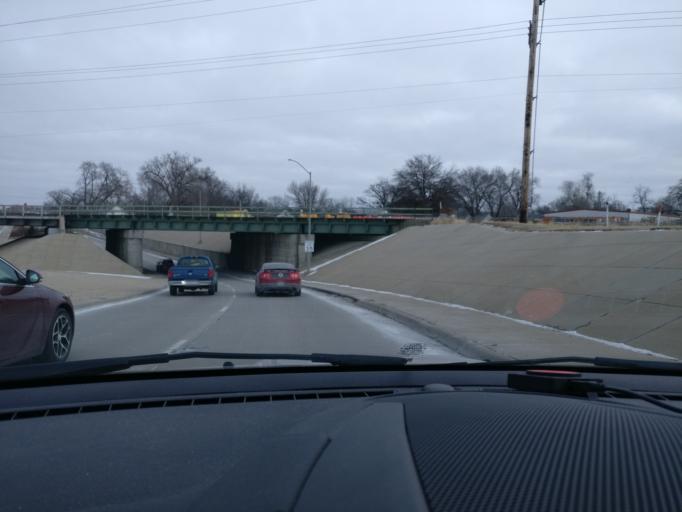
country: US
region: Nebraska
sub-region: Lancaster County
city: Lincoln
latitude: 40.8574
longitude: -96.6429
